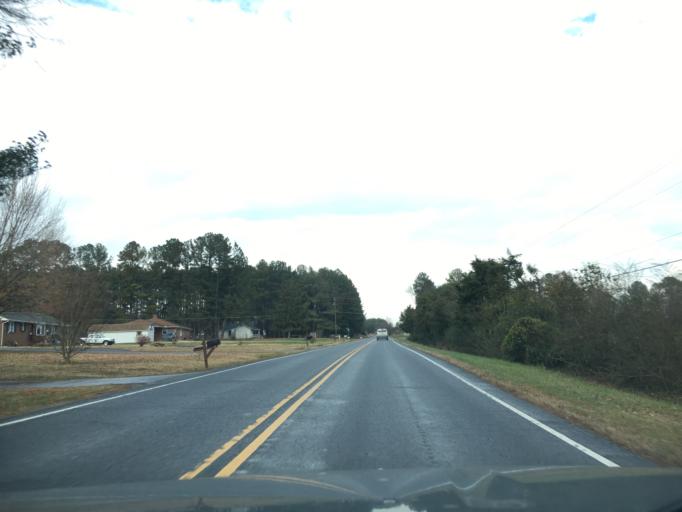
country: US
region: Virginia
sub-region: Prince Edward County
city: Farmville
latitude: 37.3273
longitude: -78.3870
